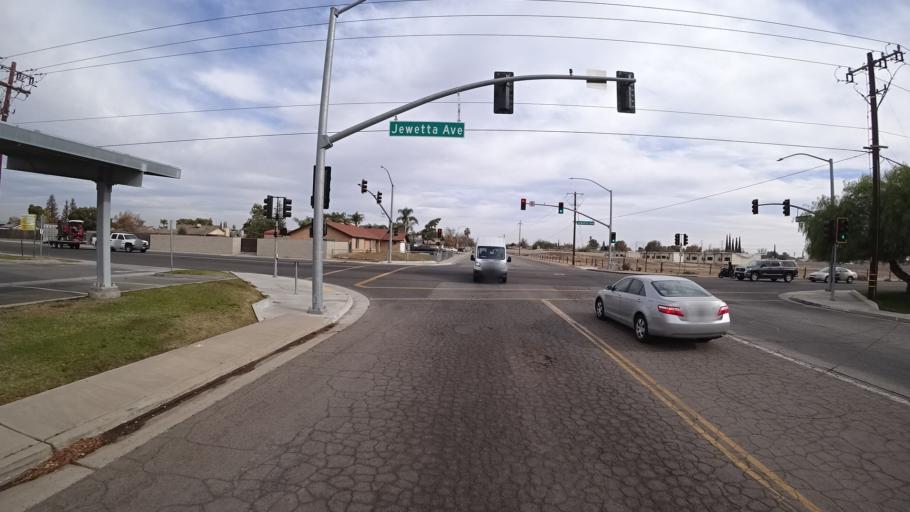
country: US
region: California
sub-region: Kern County
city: Rosedale
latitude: 35.3907
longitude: -119.1281
